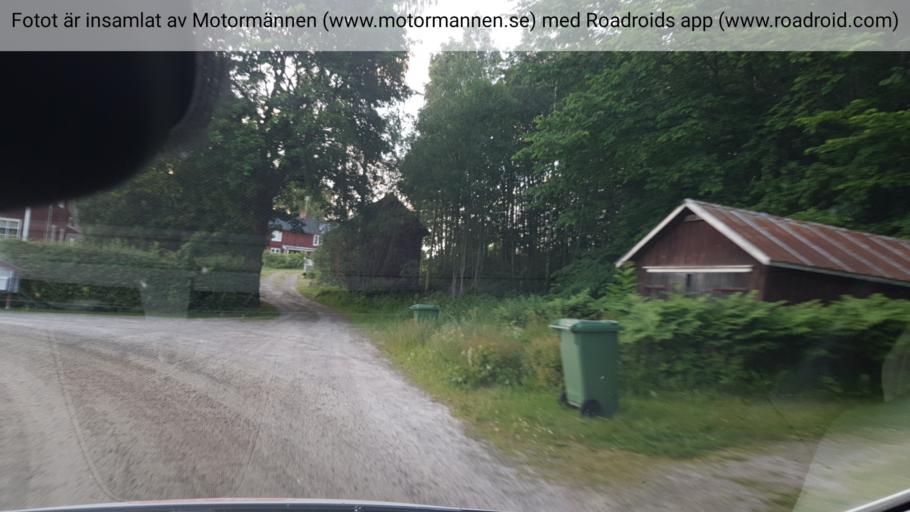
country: SE
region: Vaermland
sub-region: Sunne Kommun
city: Sunne
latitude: 59.7058
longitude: 12.8856
